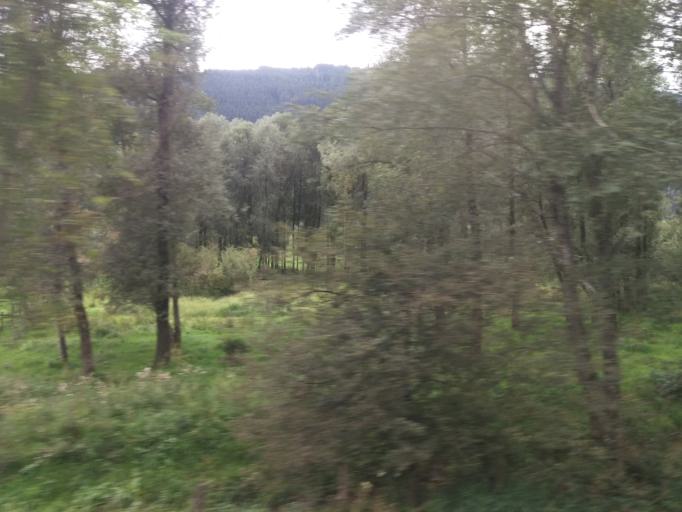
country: AT
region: Salzburg
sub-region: Politischer Bezirk Zell am See
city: Uttendorf
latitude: 47.2838
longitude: 12.5481
